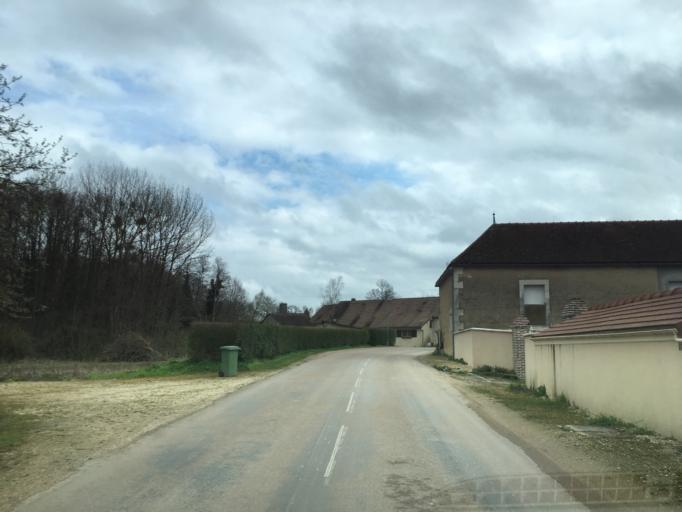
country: FR
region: Bourgogne
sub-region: Departement de l'Yonne
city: Pourrain
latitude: 47.7954
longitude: 3.3837
